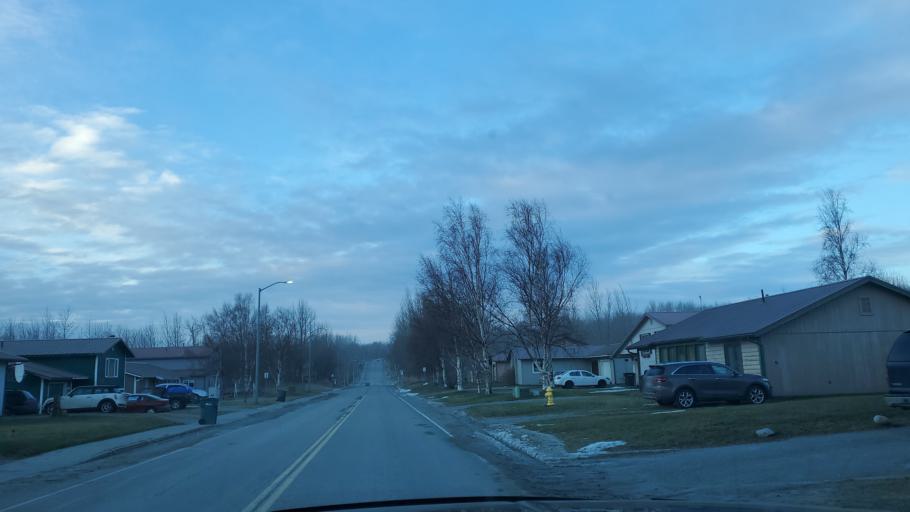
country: US
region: Alaska
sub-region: Matanuska-Susitna Borough
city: Palmer
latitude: 61.6139
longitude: -149.1043
